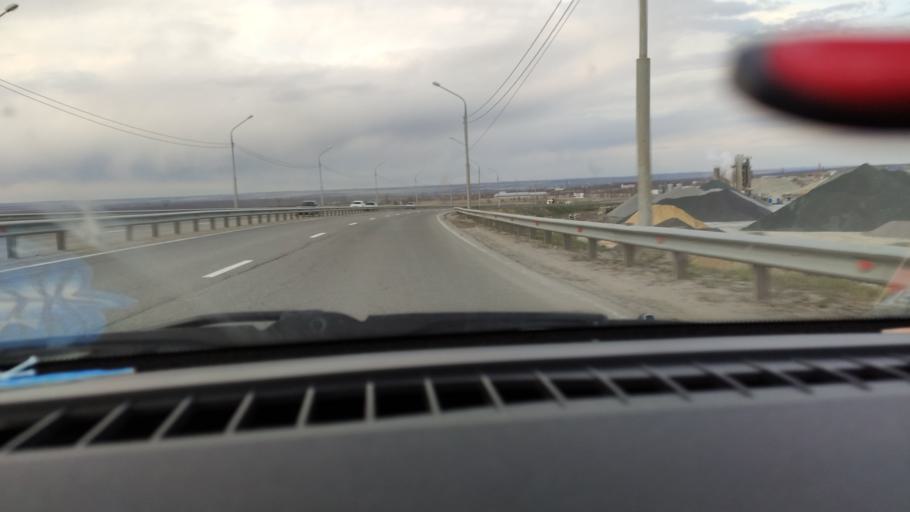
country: RU
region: Saratov
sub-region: Saratovskiy Rayon
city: Saratov
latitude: 51.6478
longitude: 45.9901
